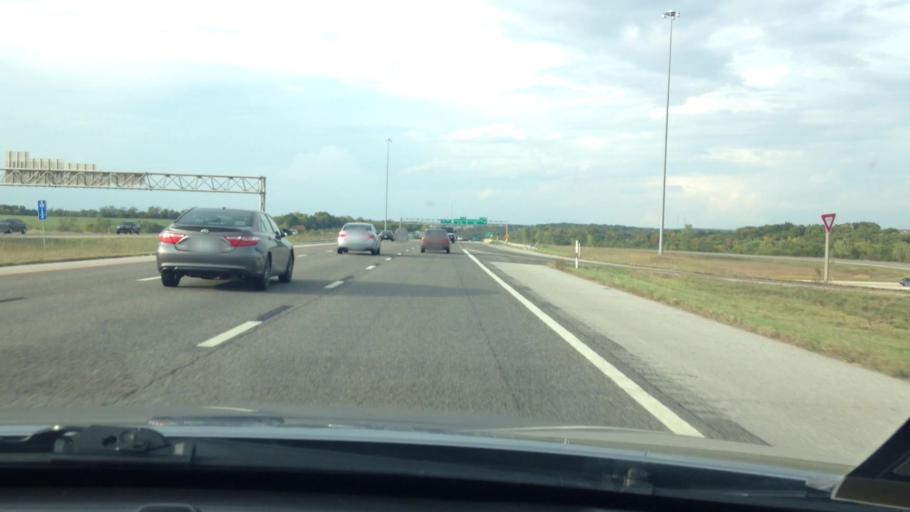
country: US
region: Kansas
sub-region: Wyandotte County
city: Edwardsville
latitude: 39.1411
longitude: -94.8196
